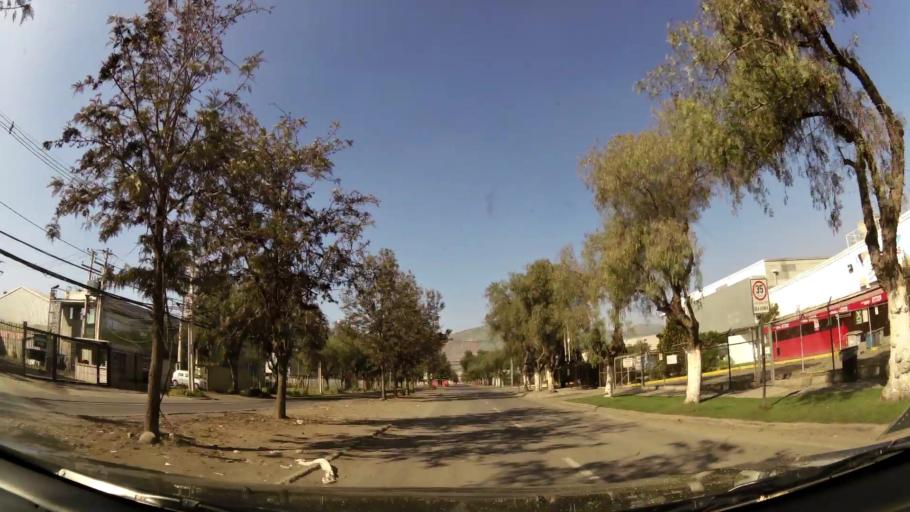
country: CL
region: Santiago Metropolitan
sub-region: Provincia de Chacabuco
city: Chicureo Abajo
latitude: -33.3282
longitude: -70.7250
